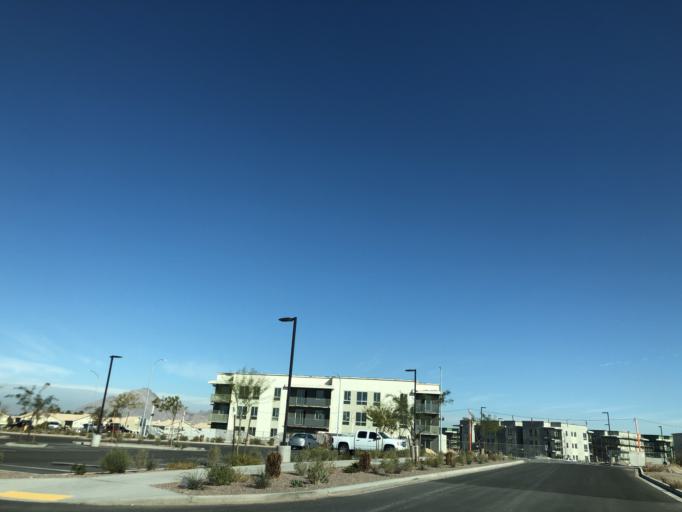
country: US
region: Nevada
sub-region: Clark County
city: Whitney
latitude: 36.0760
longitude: -115.0361
